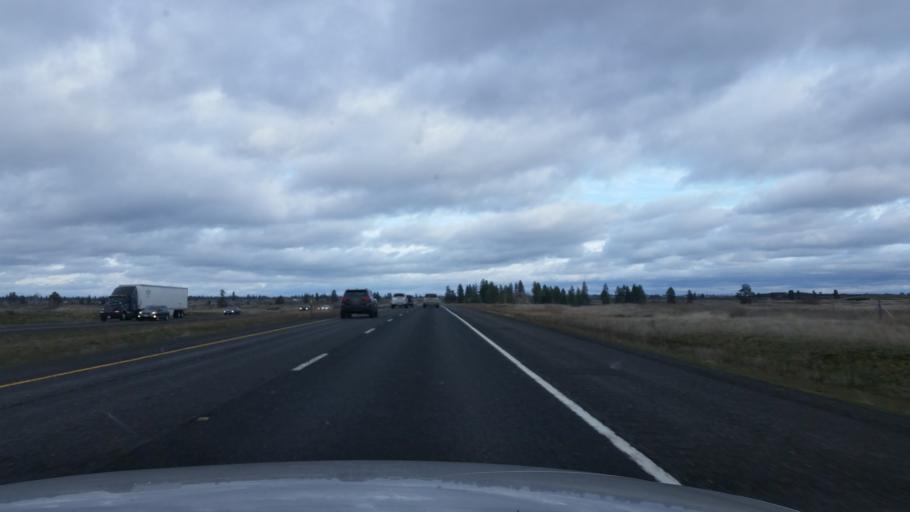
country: US
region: Washington
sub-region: Spokane County
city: Medical Lake
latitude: 47.3863
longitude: -117.8562
